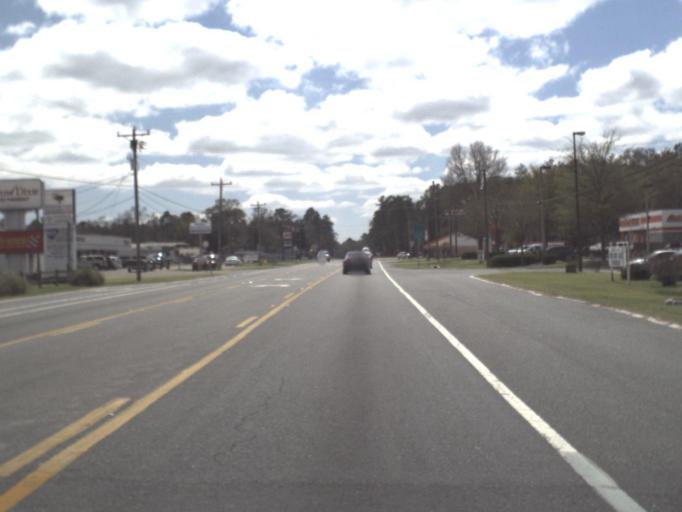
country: US
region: Florida
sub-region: Wakulla County
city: Crawfordville
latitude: 30.1929
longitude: -84.3717
